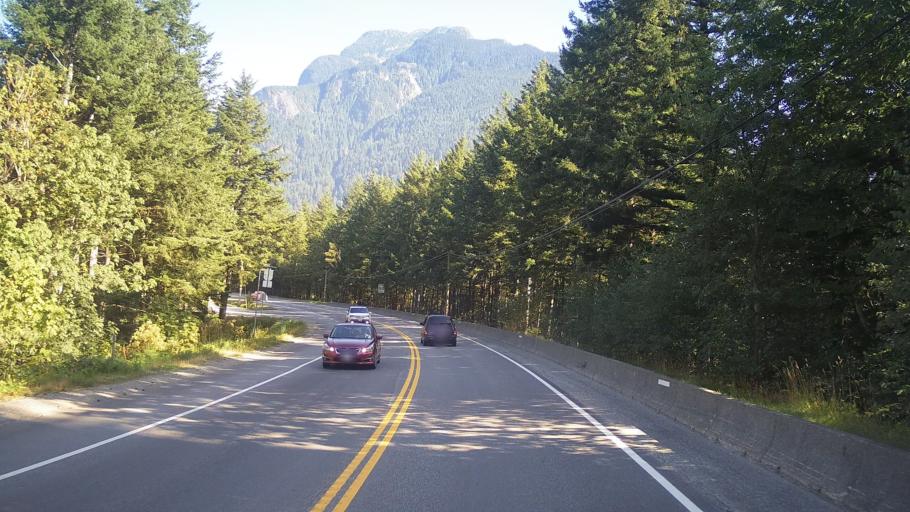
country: CA
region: British Columbia
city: Hope
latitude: 49.3876
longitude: -121.4609
